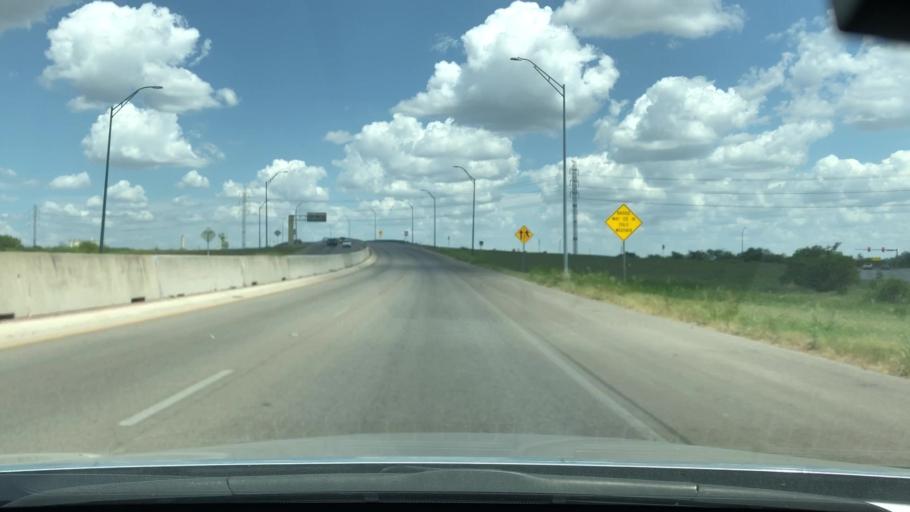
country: US
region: Texas
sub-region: Bexar County
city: Windcrest
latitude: 29.5452
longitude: -98.4366
